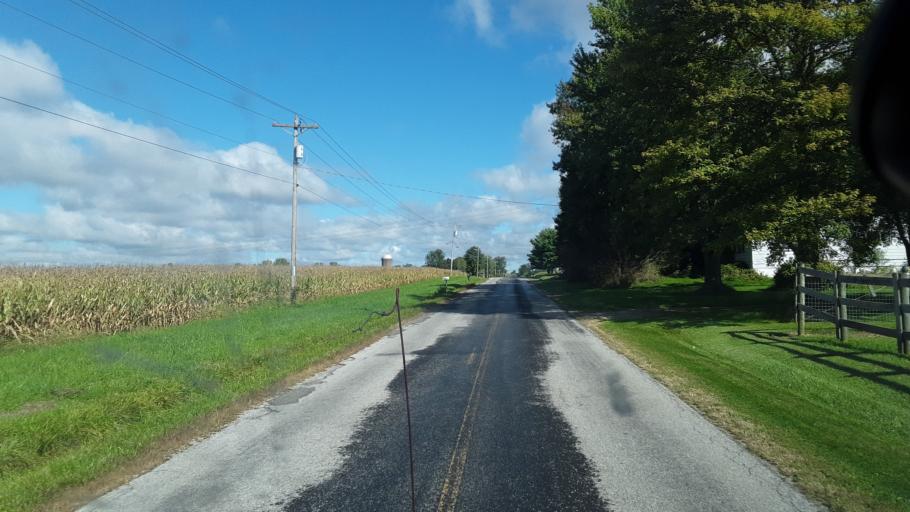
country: US
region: Ohio
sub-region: Licking County
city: Johnstown
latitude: 40.2096
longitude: -82.7557
